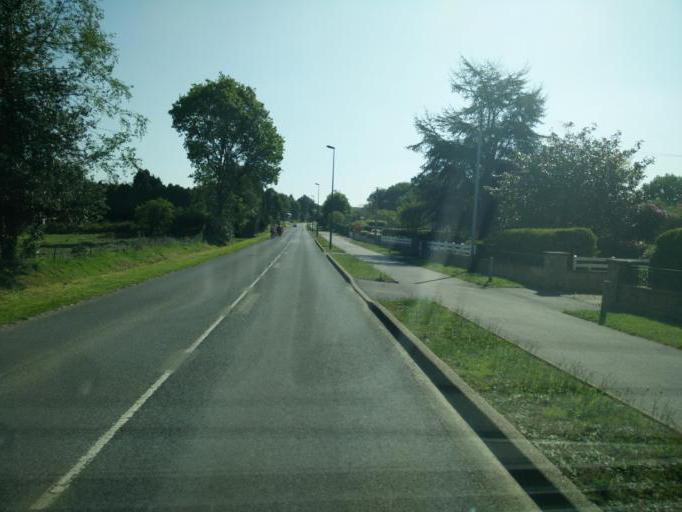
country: FR
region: Brittany
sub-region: Departement du Morbihan
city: Languidic
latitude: 47.8337
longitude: -3.1715
